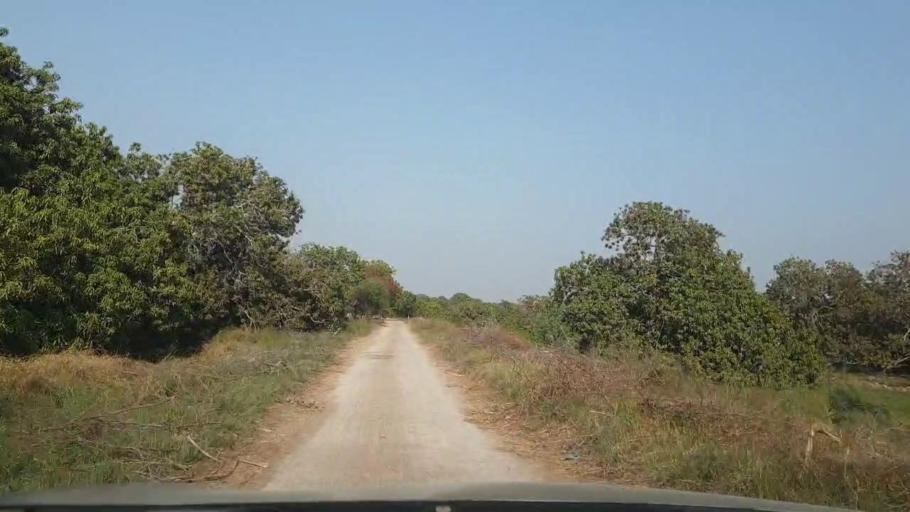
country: PK
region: Sindh
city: Tando Allahyar
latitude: 25.5944
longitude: 68.8129
